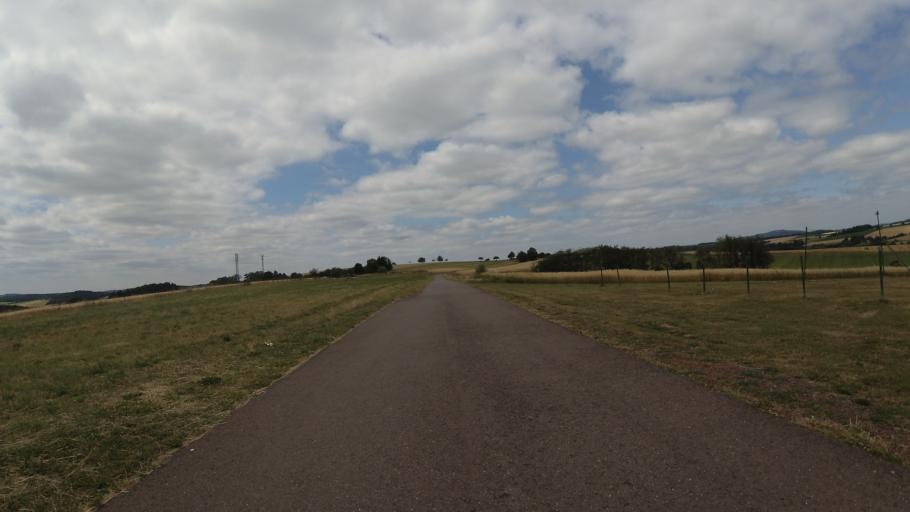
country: DE
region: Saarland
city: Mainzweiler
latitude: 49.4215
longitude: 7.0969
